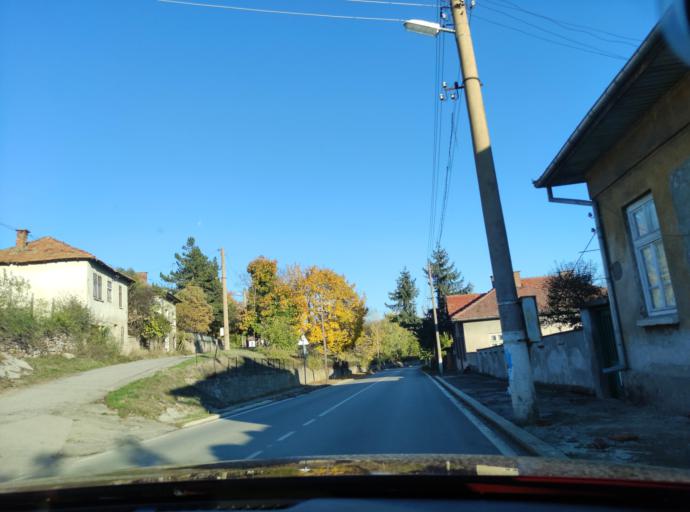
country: BG
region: Montana
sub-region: Obshtina Chiprovtsi
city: Chiprovtsi
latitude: 43.4341
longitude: 22.9713
